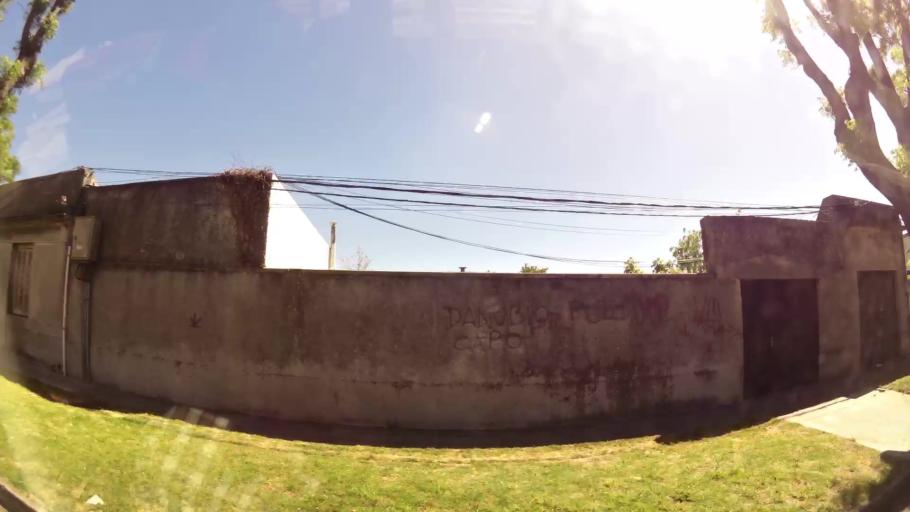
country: UY
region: Canelones
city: Paso de Carrasco
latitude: -34.8523
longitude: -56.1288
